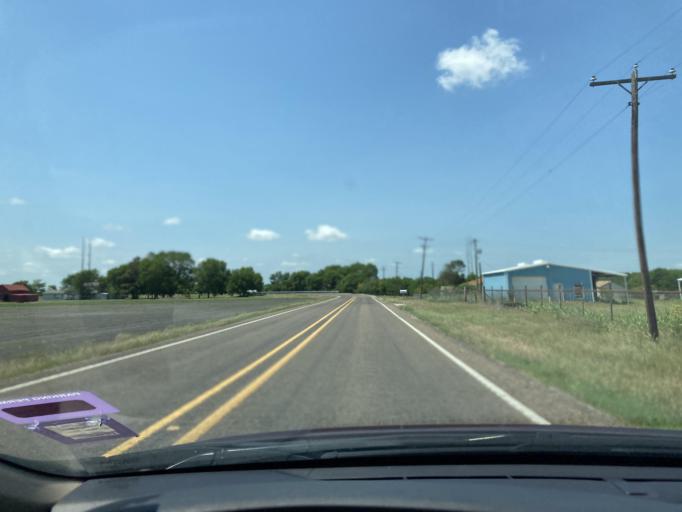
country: US
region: Texas
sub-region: Navarro County
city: Kerens
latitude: 32.1090
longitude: -96.3216
